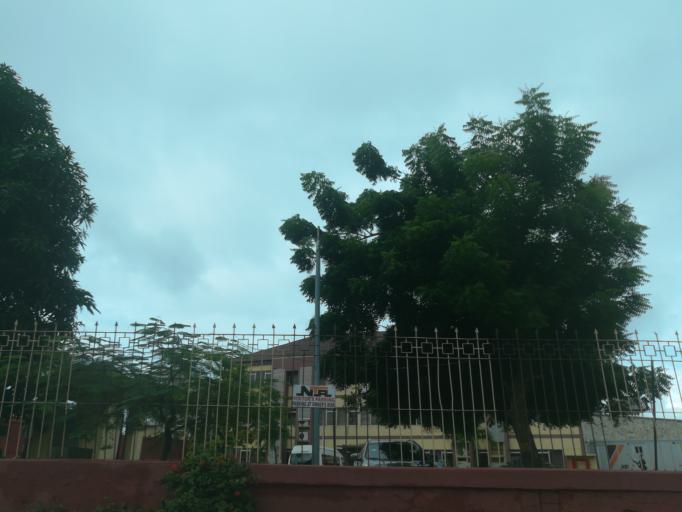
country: NG
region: Lagos
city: Lagos
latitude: 6.4243
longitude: 3.4098
